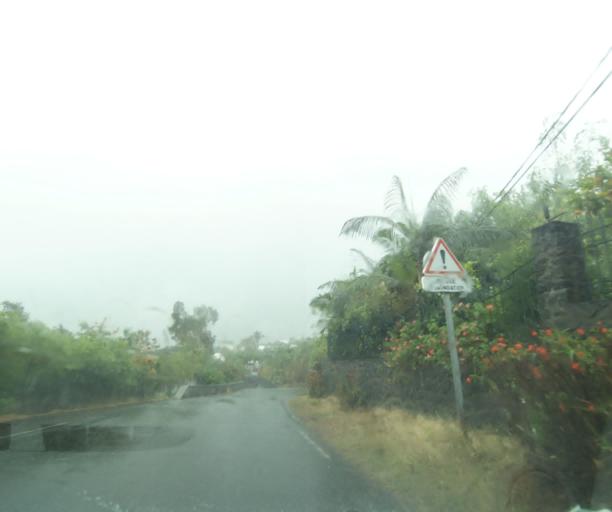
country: RE
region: Reunion
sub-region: Reunion
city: La Possession
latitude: -20.9853
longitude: 55.3254
